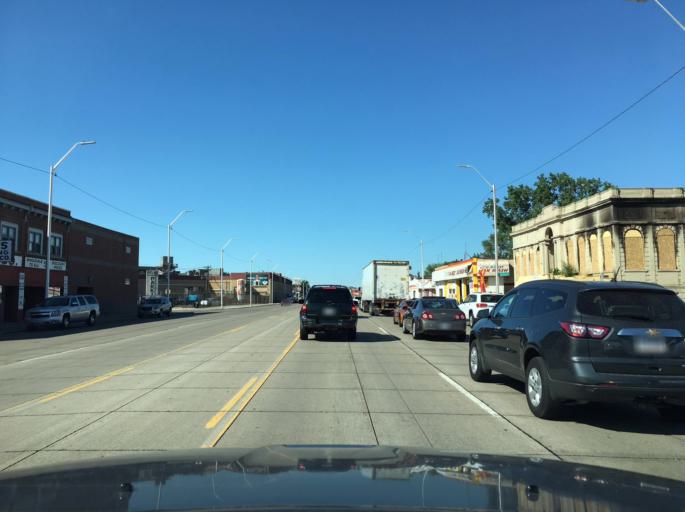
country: US
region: Michigan
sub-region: Wayne County
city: Detroit
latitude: 42.3604
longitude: -83.0268
